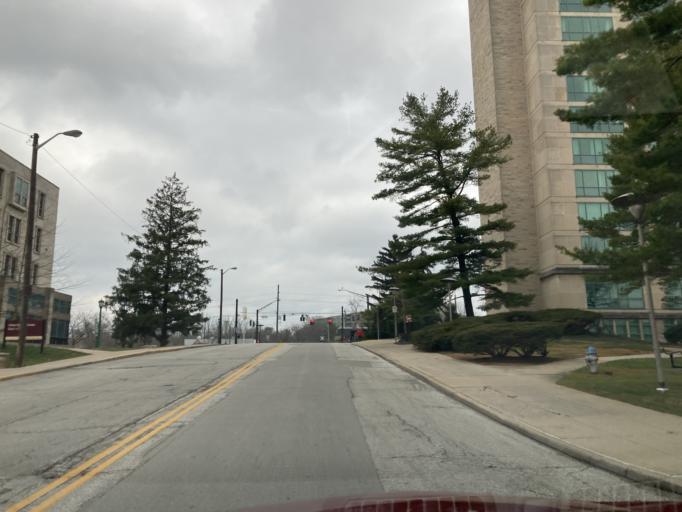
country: US
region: Indiana
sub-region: Monroe County
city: Bloomington
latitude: 39.1705
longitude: -86.5095
